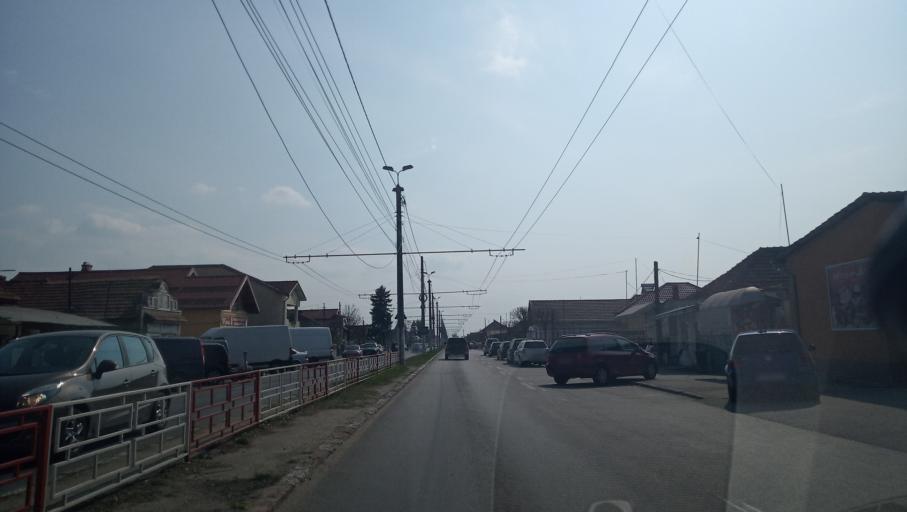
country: RO
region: Gorj
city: Targu Jiu
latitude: 45.0637
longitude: 23.2915
